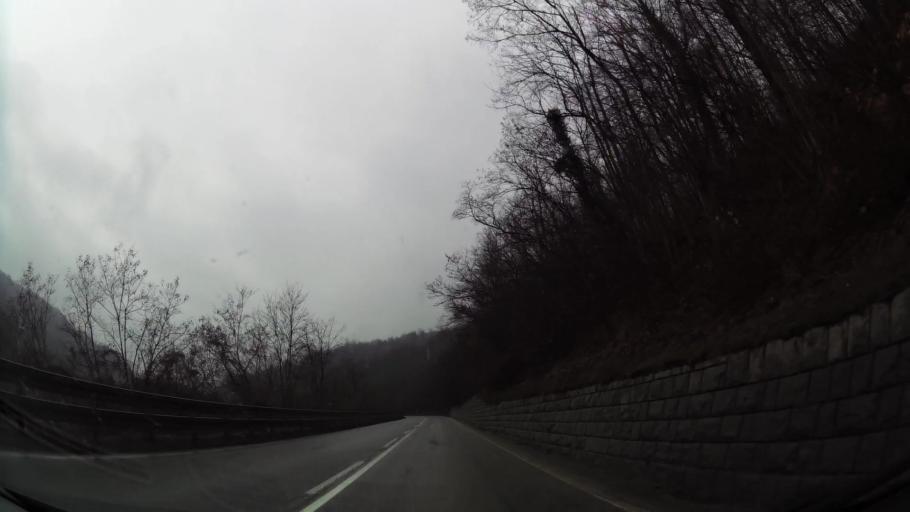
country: RS
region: Central Serbia
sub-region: Jablanicki Okrug
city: Vlasotince
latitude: 42.8435
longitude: 22.1363
